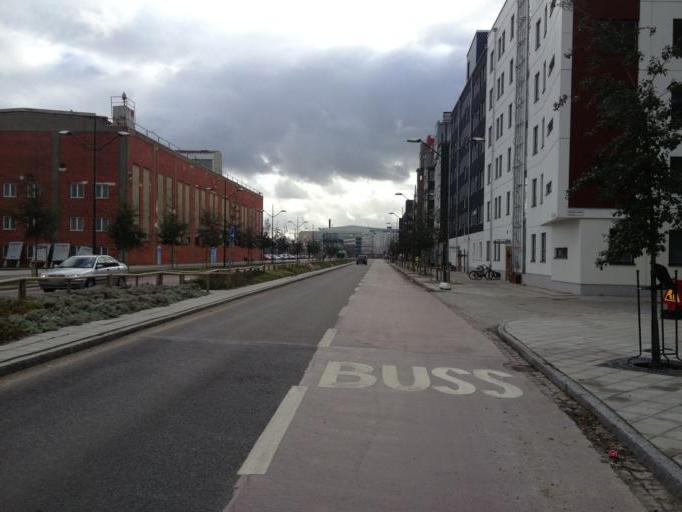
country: SE
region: Skane
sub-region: Malmo
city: Malmoe
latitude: 55.6173
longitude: 12.9829
